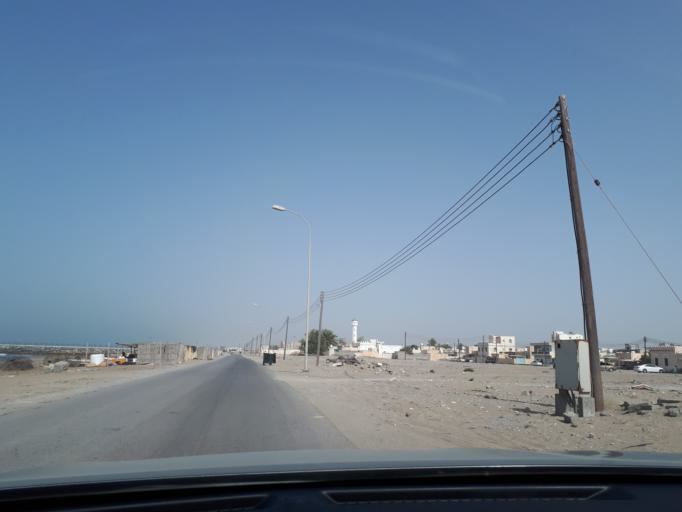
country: OM
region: Al Batinah
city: Barka'
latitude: 23.7106
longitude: 57.8869
